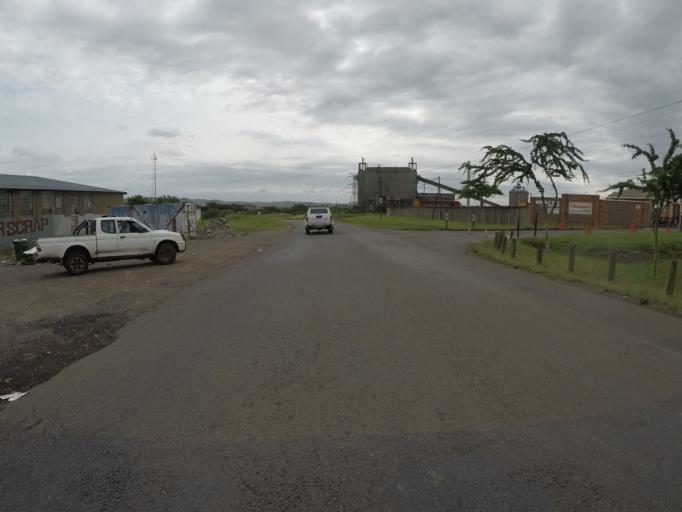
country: ZA
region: KwaZulu-Natal
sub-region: uThungulu District Municipality
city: Empangeni
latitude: -28.7247
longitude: 31.8666
